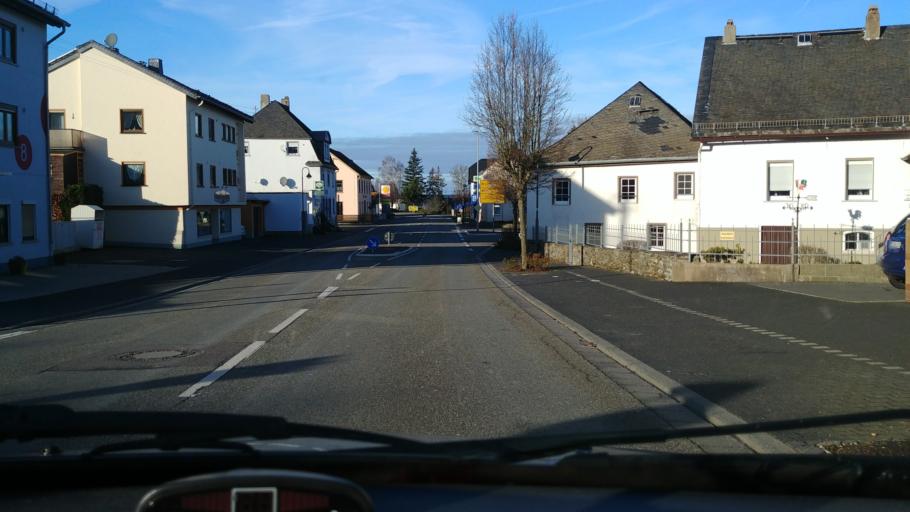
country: DE
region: Rheinland-Pfalz
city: Holzhausen an der Haide
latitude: 50.2195
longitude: 7.9057
